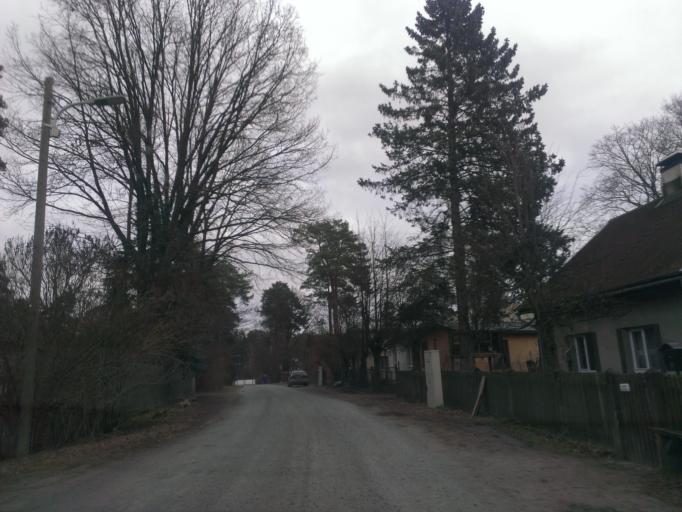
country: LV
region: Riga
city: Bergi
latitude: 56.9898
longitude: 24.3014
